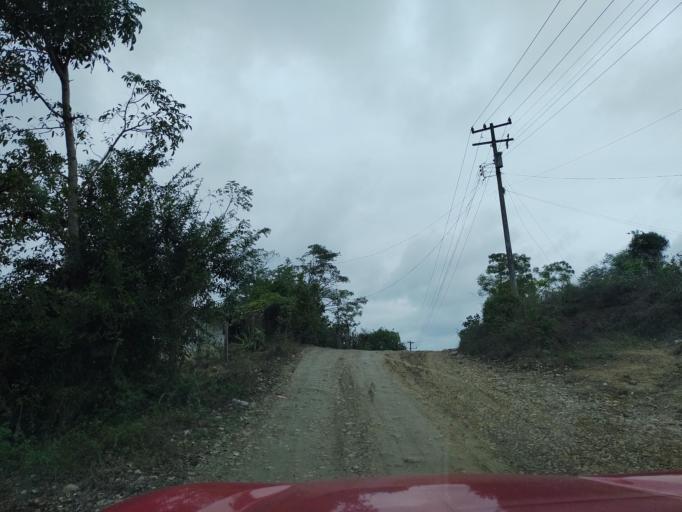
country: MX
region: Veracruz
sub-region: Coatzintla
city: Manuel Maria Contreras
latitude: 20.4107
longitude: -97.4575
